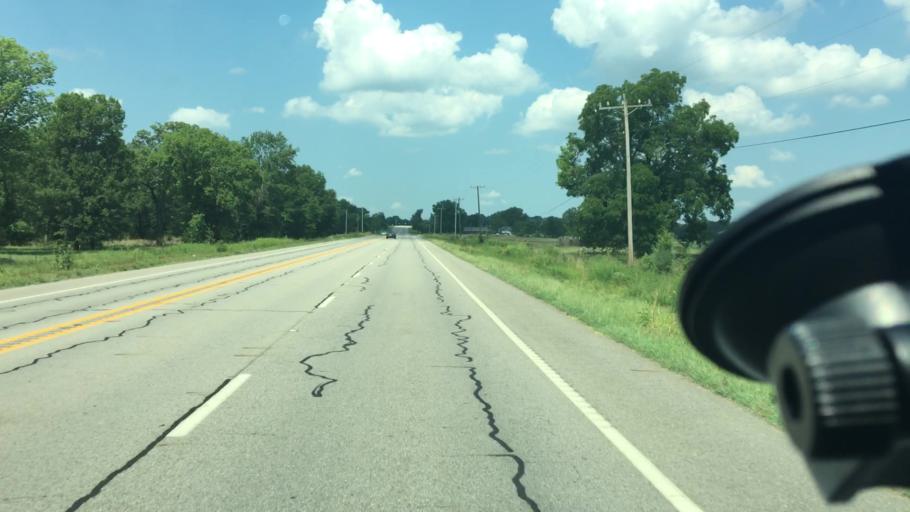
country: US
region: Arkansas
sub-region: Logan County
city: Paris
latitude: 35.2986
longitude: -93.8172
